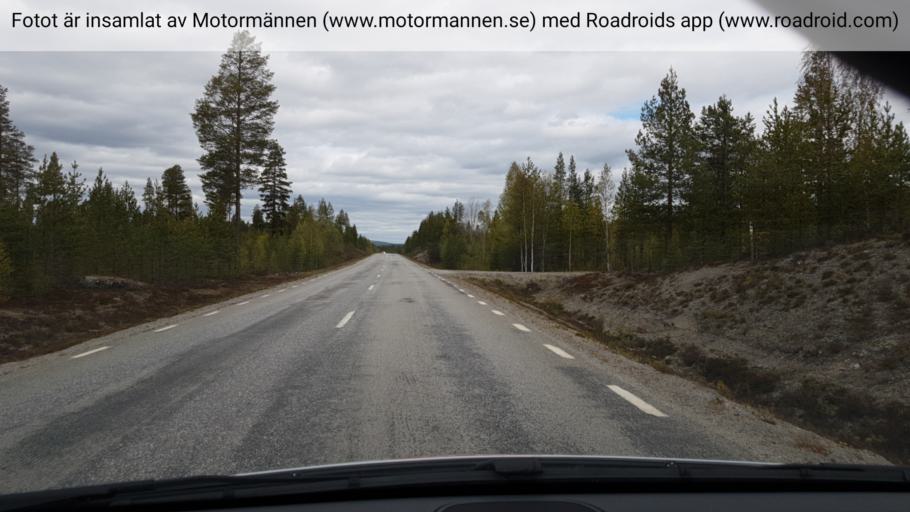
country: SE
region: Vaesterbotten
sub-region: Mala Kommun
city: Mala
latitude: 64.9694
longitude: 18.5784
